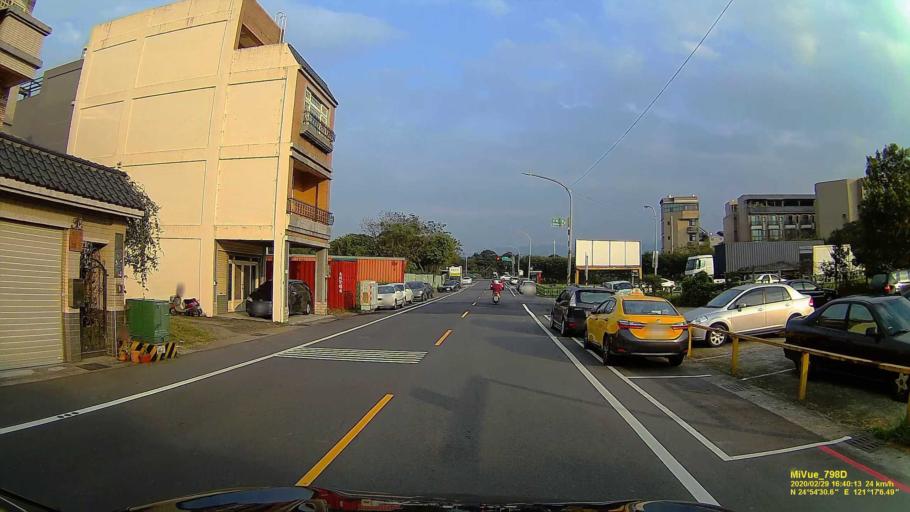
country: TW
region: Taiwan
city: Daxi
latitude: 24.9085
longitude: 121.2852
